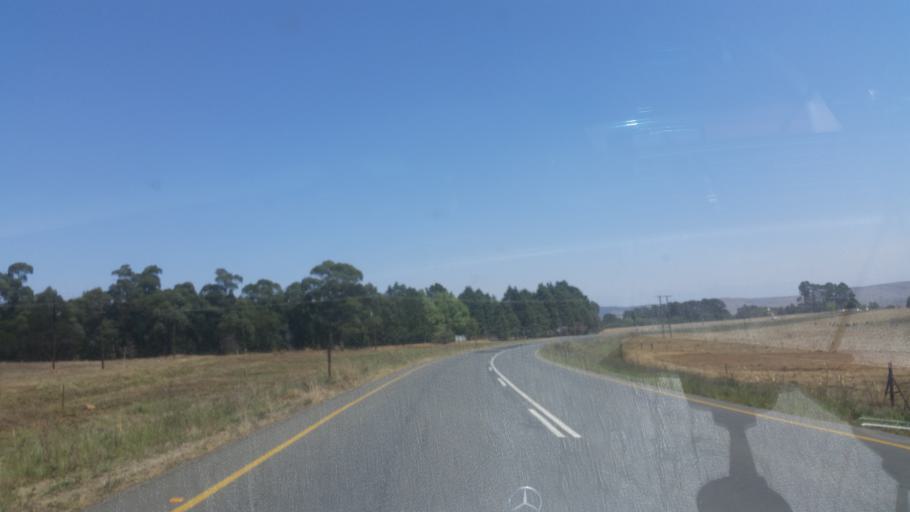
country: ZA
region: KwaZulu-Natal
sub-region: uMgungundlovu District Municipality
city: Mooirivier
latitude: -29.1489
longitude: 29.9858
